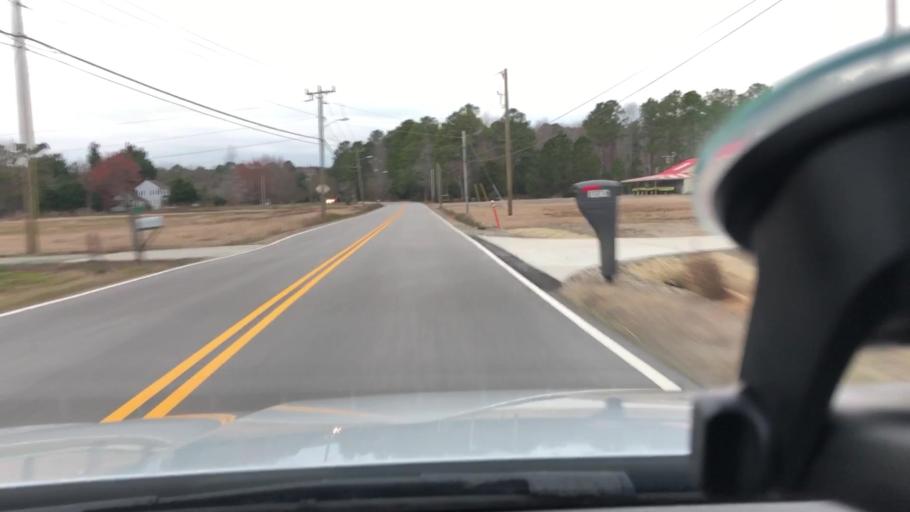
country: US
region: Virginia
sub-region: City of Virginia Beach
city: Virginia Beach
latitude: 36.7306
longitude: -75.9749
